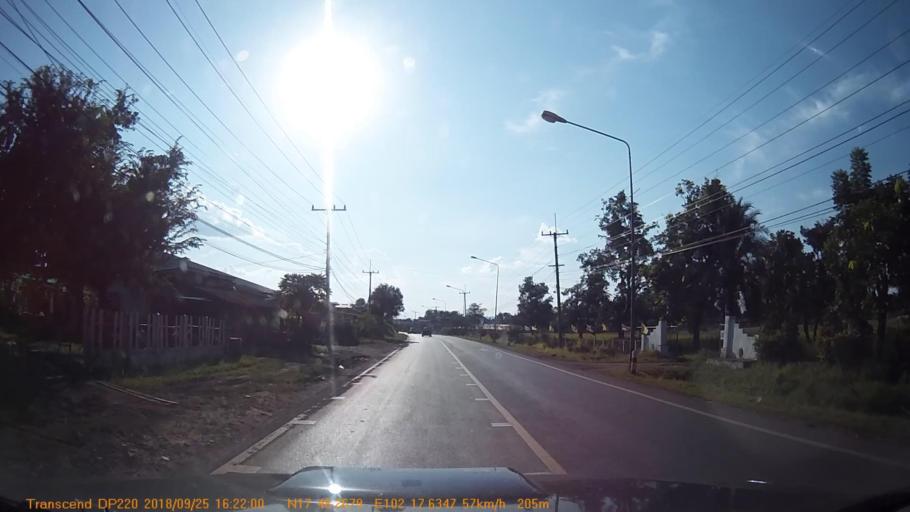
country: TH
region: Changwat Udon Thani
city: Nam Som
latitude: 17.8045
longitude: 102.2940
